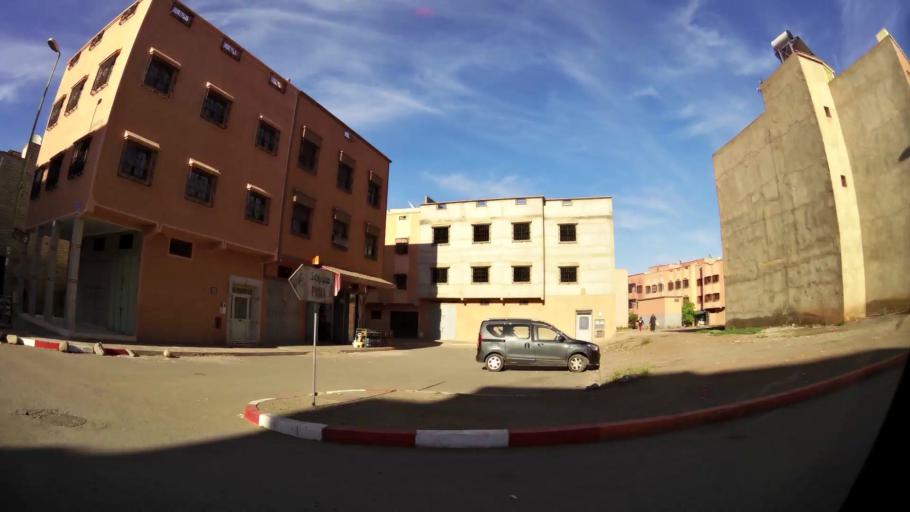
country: MA
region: Marrakech-Tensift-Al Haouz
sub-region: Marrakech
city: Marrakesh
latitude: 31.6224
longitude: -8.0691
